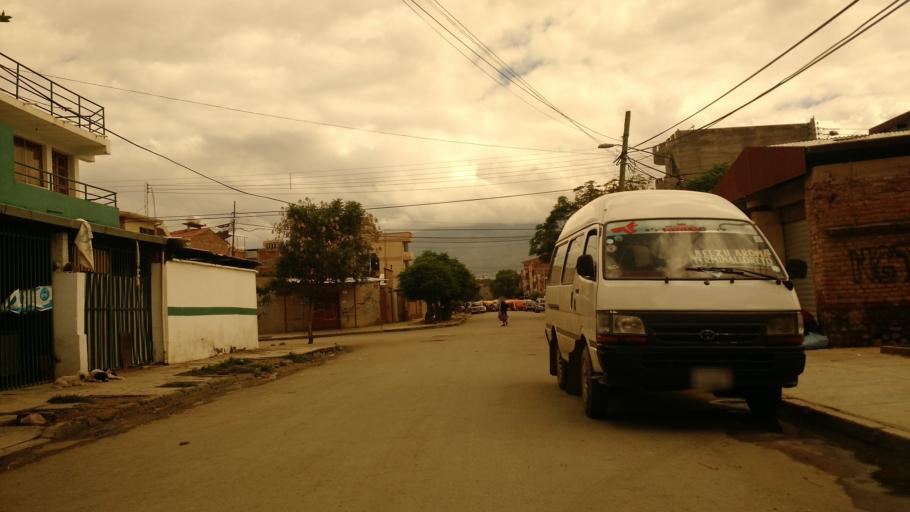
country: BO
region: Cochabamba
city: Cochabamba
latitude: -17.4231
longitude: -66.1574
